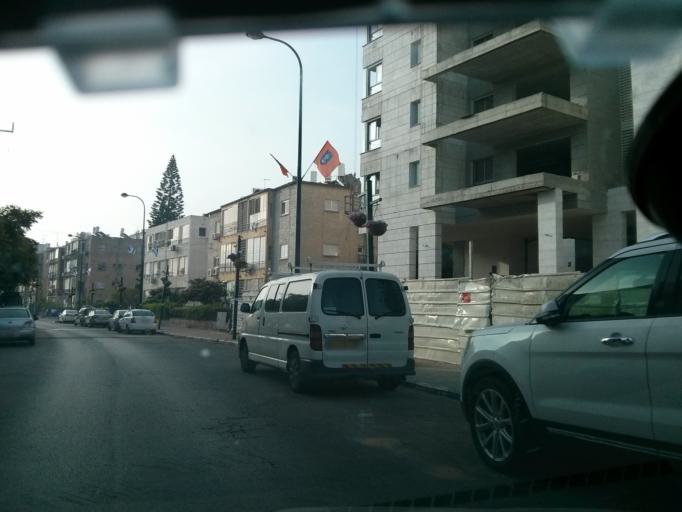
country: IL
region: Central District
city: Netanya
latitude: 32.3240
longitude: 34.8544
